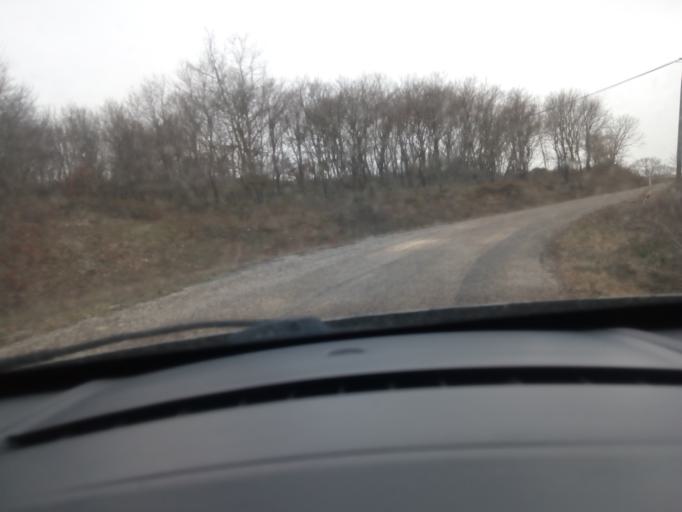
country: TR
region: Balikesir
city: Omerkoy
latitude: 39.8933
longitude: 28.0231
